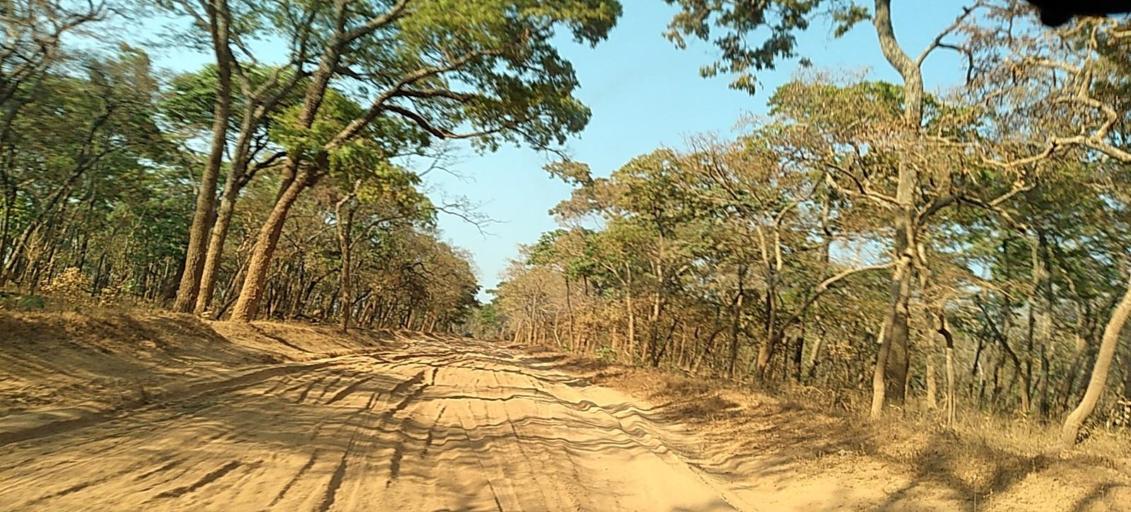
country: ZM
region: North-Western
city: Kasempa
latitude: -13.5657
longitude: 25.9966
